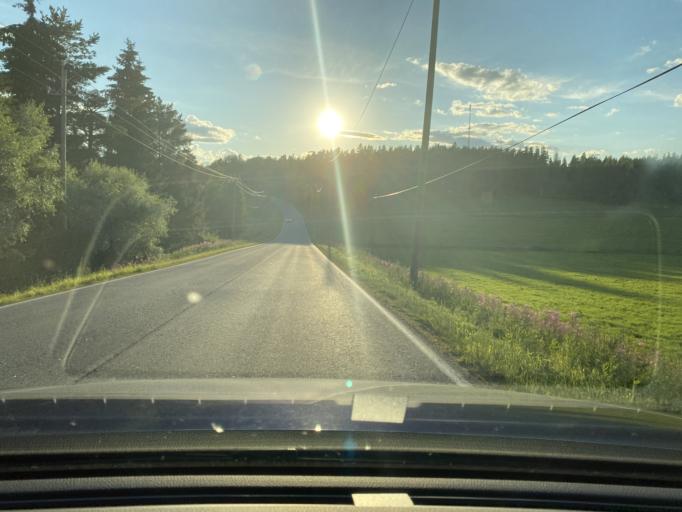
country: FI
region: Uusimaa
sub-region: Helsinki
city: Nurmijaervi
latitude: 60.4094
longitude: 24.7765
